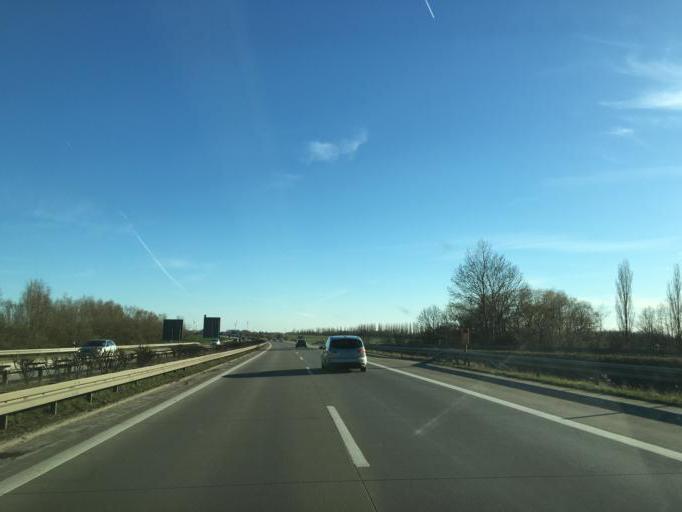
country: DE
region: Mecklenburg-Vorpommern
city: Roggentin
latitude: 54.0783
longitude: 12.1952
